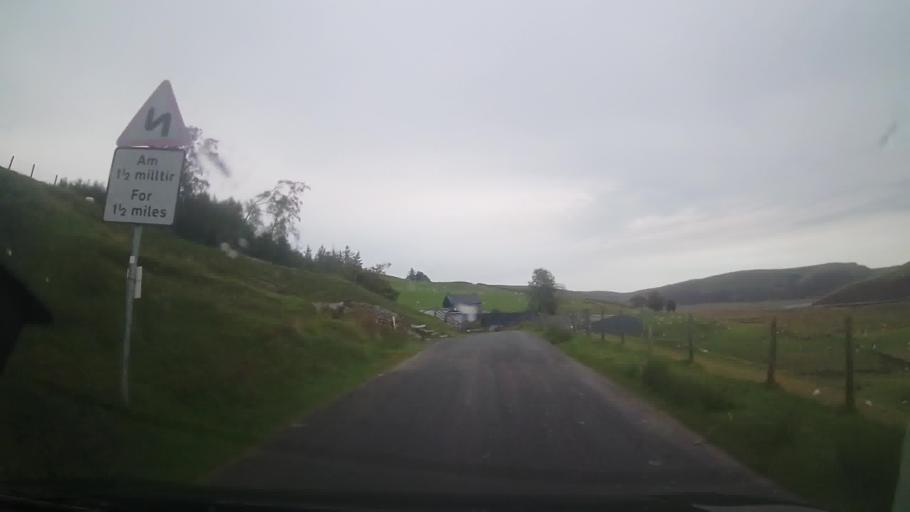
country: GB
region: Wales
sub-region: Sir Powys
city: Rhayader
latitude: 52.3149
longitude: -3.6323
